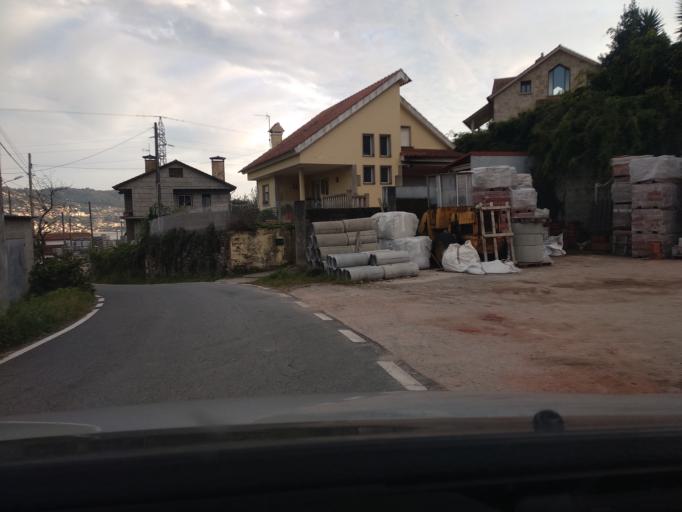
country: ES
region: Galicia
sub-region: Provincia de Pontevedra
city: Moana
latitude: 42.2937
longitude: -8.6822
